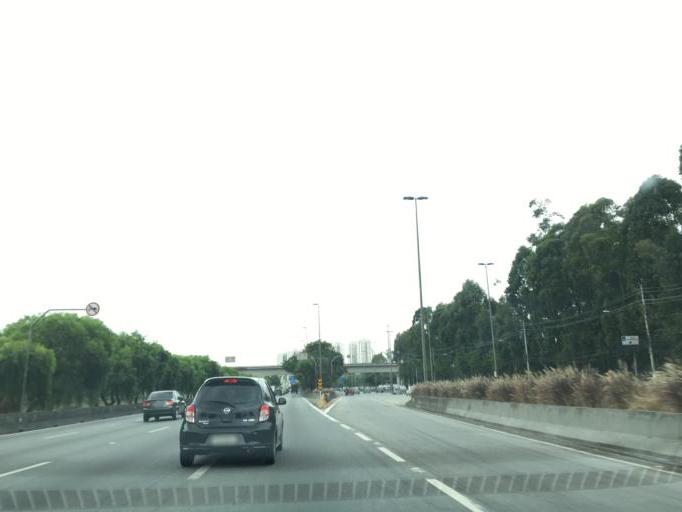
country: BR
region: Sao Paulo
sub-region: Osasco
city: Osasco
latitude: -23.5182
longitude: -46.7387
